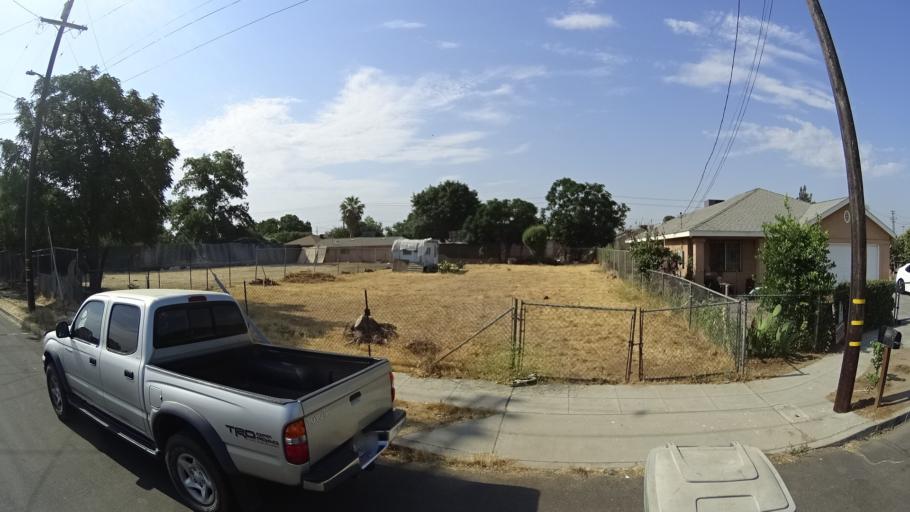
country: US
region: California
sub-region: Fresno County
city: West Park
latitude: 36.7195
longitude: -119.8167
